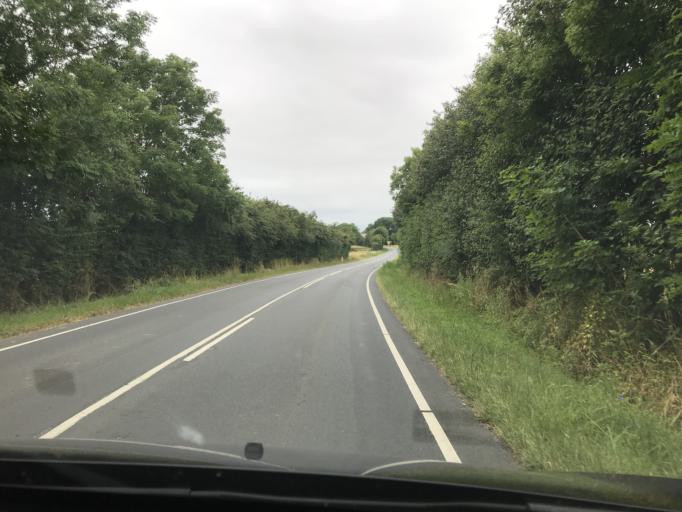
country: DK
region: South Denmark
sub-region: AEro Kommune
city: AEroskobing
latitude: 54.8769
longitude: 10.3437
